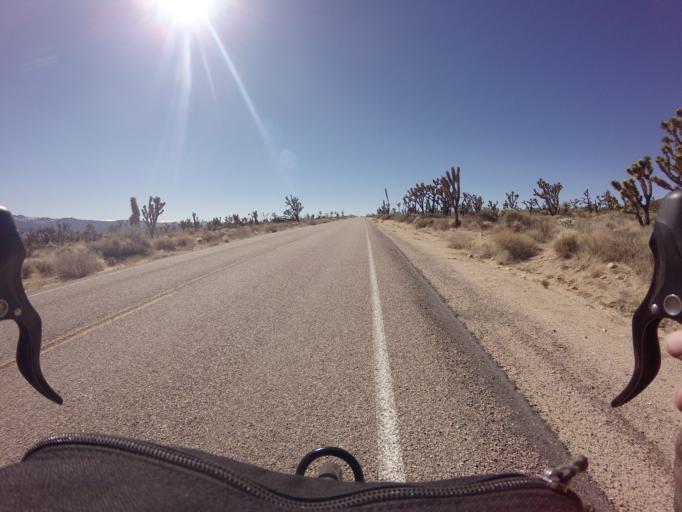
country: US
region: Nevada
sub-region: Clark County
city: Sandy Valley
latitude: 35.2920
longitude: -115.4947
